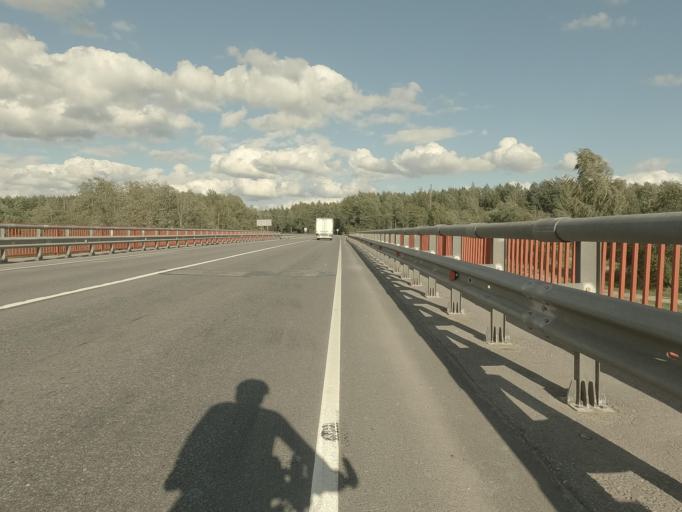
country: RU
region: Leningrad
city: Ul'yanovka
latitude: 59.6284
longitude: 30.8014
